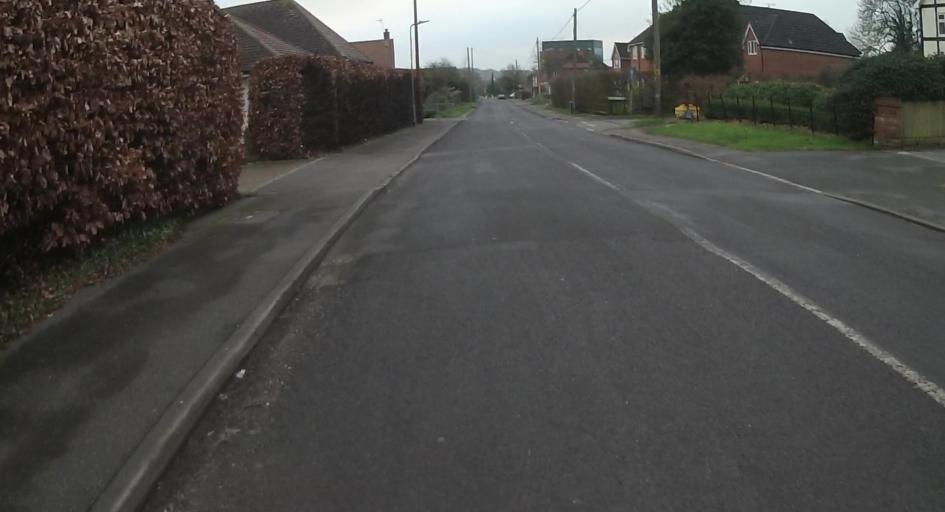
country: GB
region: England
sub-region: Bracknell Forest
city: Binfield
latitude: 51.4177
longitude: -0.7856
